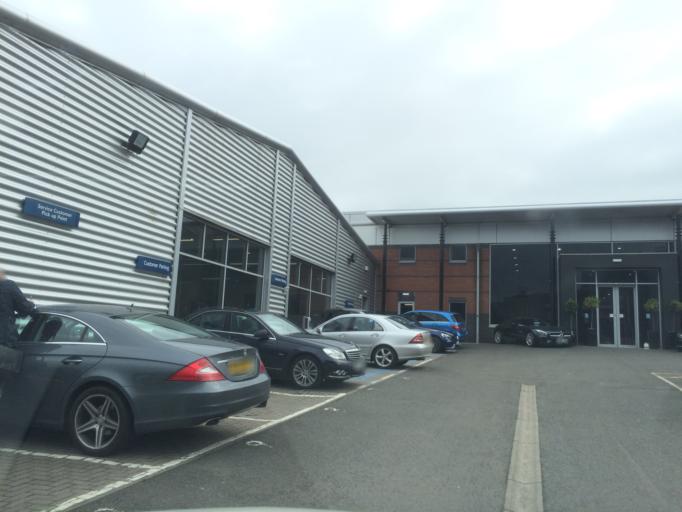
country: GB
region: Scotland
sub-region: Glasgow City
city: Glasgow
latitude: 55.8685
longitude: -4.2518
